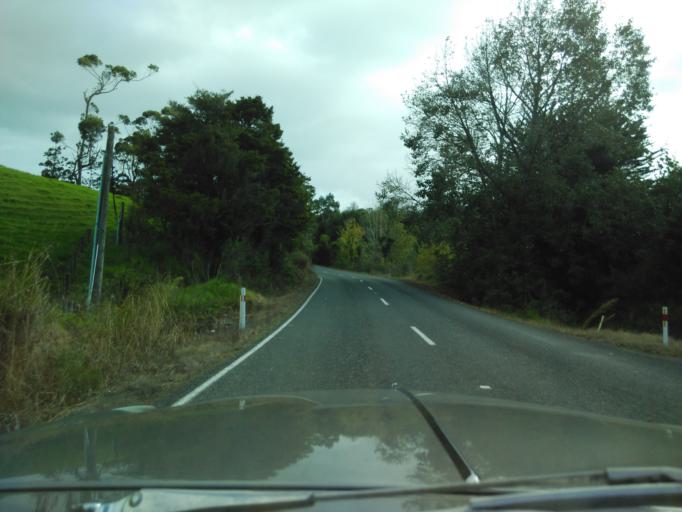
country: NZ
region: Auckland
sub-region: Auckland
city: Wellsford
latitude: -36.1637
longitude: 174.4349
